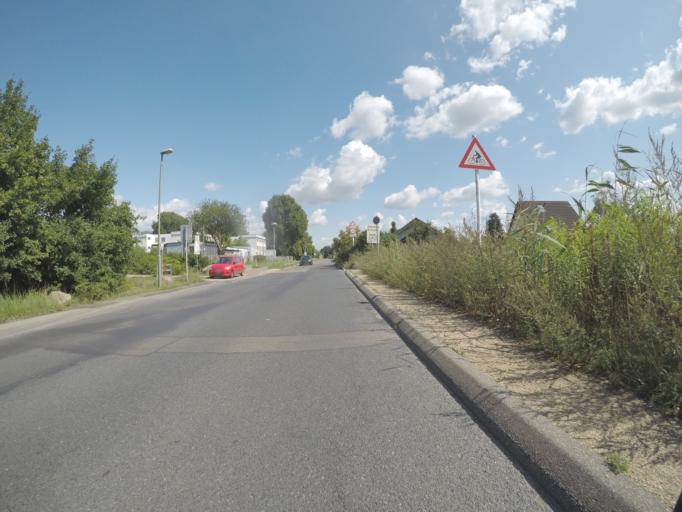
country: DE
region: Berlin
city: Mahlsdorf
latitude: 52.5011
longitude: 13.6064
